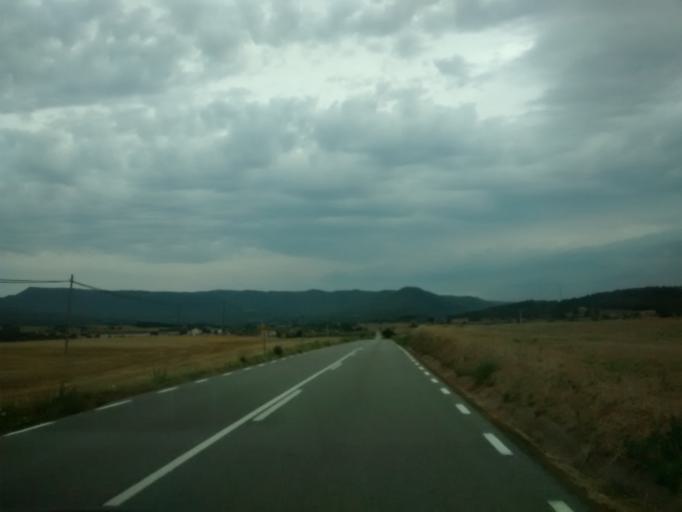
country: ES
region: Catalonia
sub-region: Provincia de Barcelona
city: Rajadell
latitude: 41.7504
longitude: 1.7224
